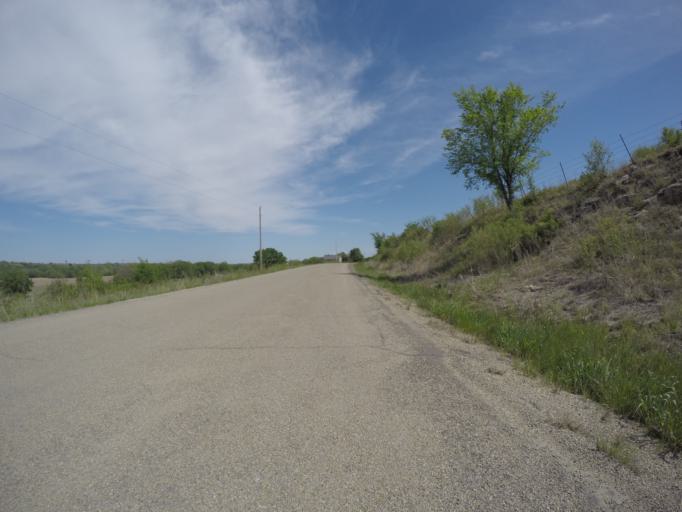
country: US
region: Kansas
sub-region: Riley County
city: Ogden
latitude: 39.0466
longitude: -96.6386
